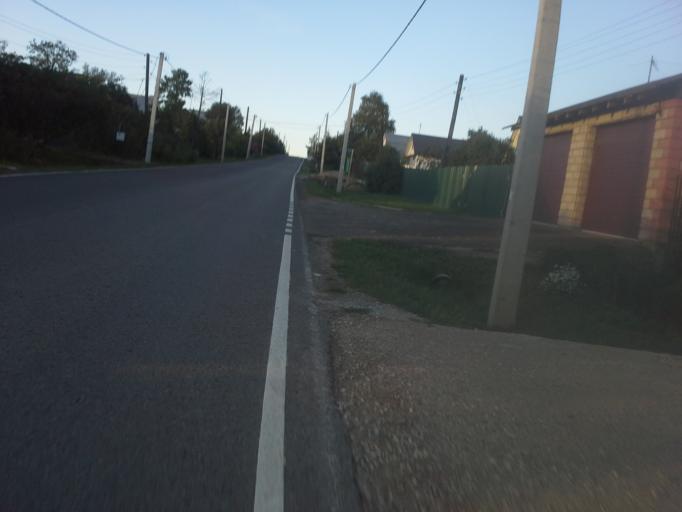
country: RU
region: Moskovskaya
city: Selyatino
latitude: 55.4997
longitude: 36.9257
